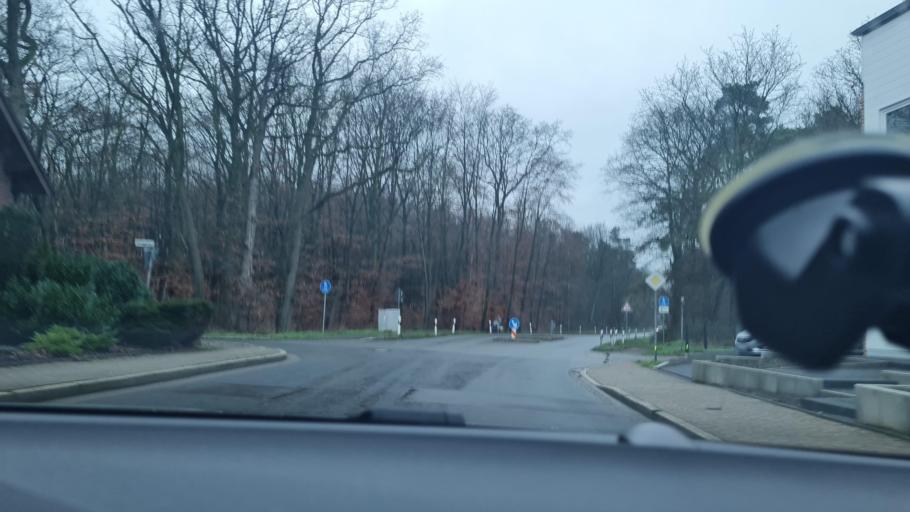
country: DE
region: North Rhine-Westphalia
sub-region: Regierungsbezirk Munster
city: Heiden
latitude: 51.7557
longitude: 6.9288
